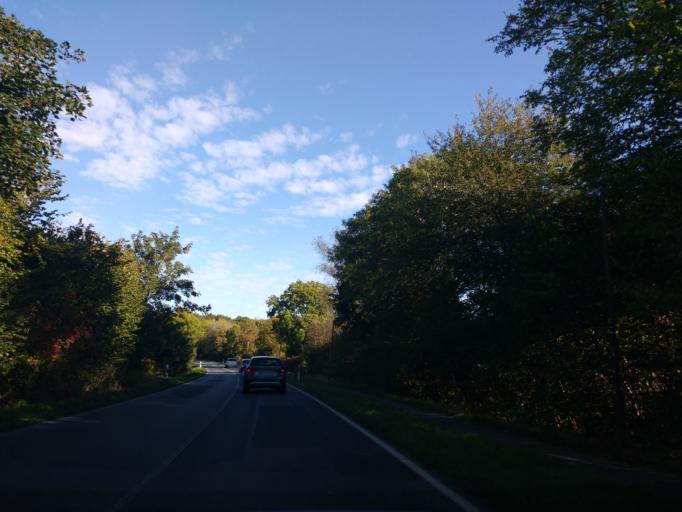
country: DE
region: Schleswig-Holstein
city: Ratekau
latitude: 53.9573
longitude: 10.7582
